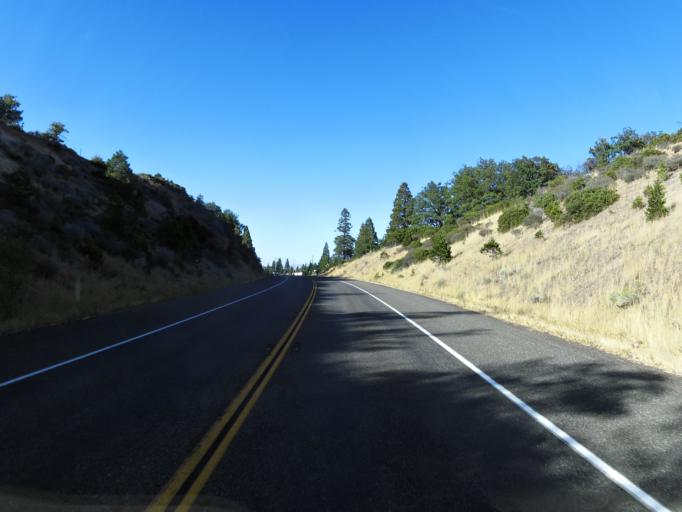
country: US
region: California
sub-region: Siskiyou County
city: Weed
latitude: 41.4336
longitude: -122.3875
